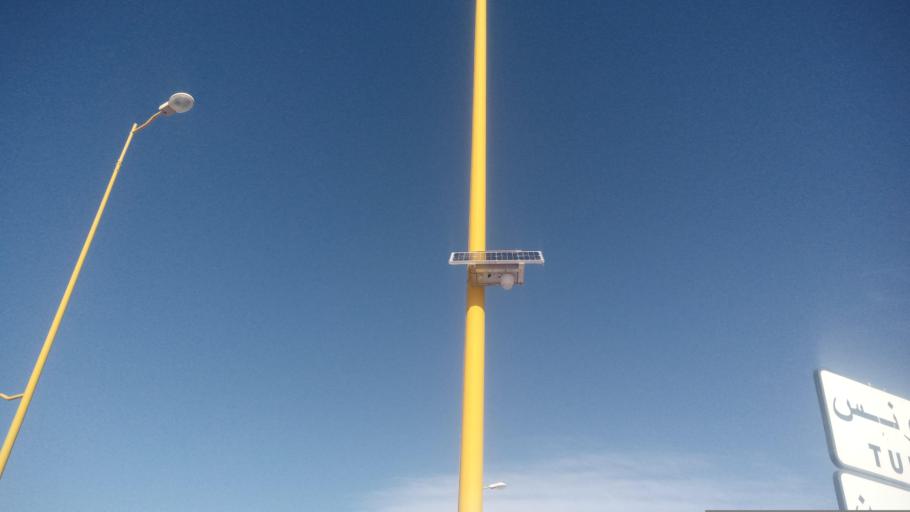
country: TN
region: Tataouine
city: Tataouine
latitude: 32.9698
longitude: 10.4605
